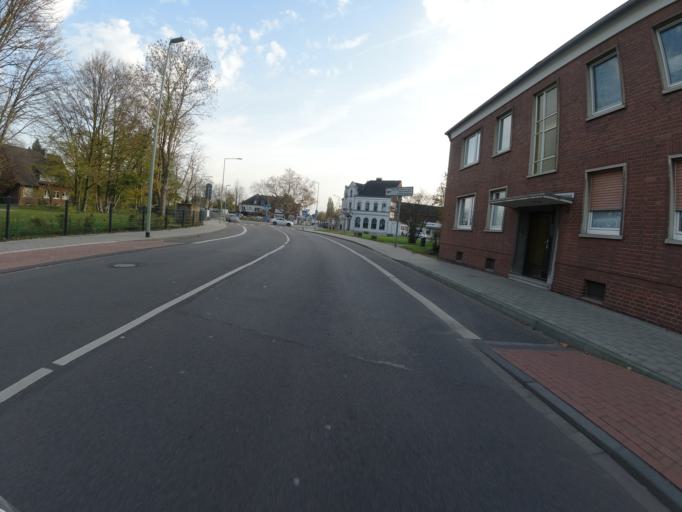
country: DE
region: North Rhine-Westphalia
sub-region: Regierungsbezirk Dusseldorf
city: Moers
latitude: 51.4107
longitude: 6.6834
